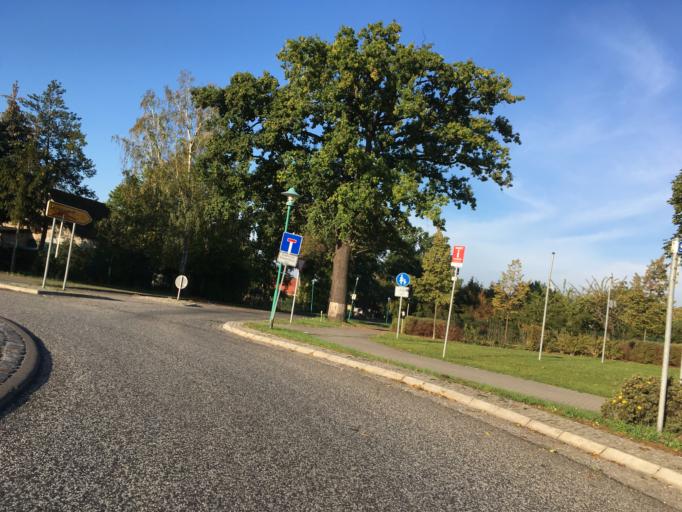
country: DE
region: Brandenburg
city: Lebus
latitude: 52.4268
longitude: 14.5326
